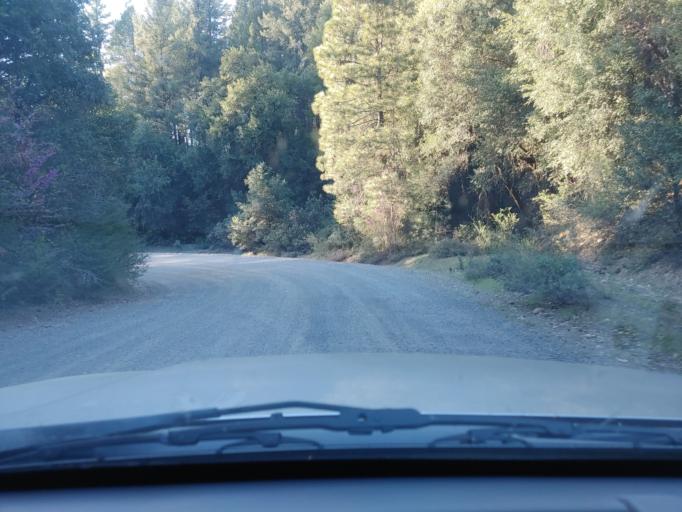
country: US
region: California
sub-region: Shasta County
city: Bella Vista
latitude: 40.8222
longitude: -122.0166
